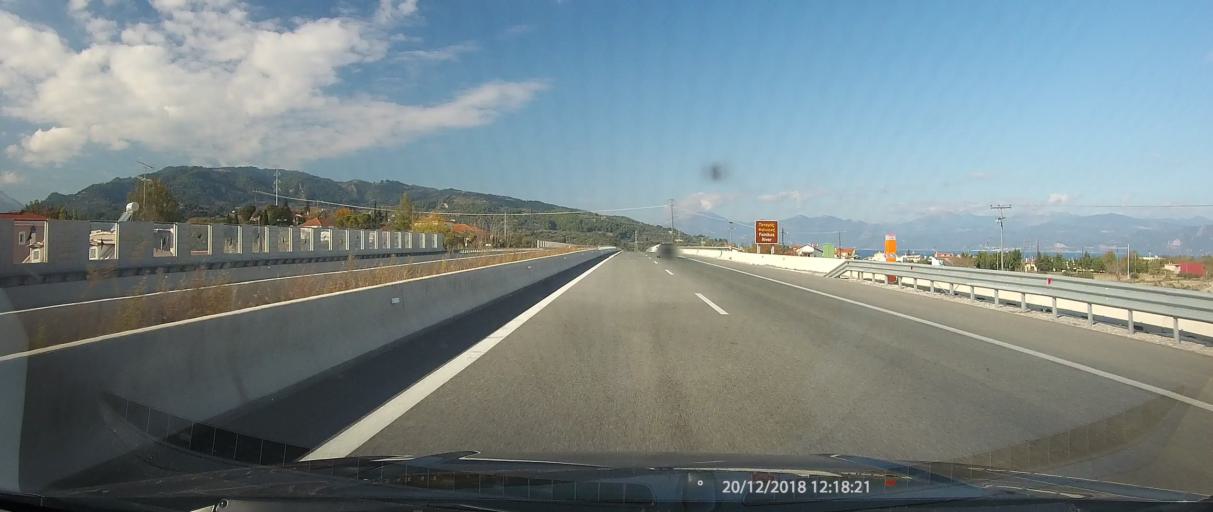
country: GR
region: West Greece
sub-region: Nomos Achaias
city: Kamarai
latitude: 38.2965
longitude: 22.0046
